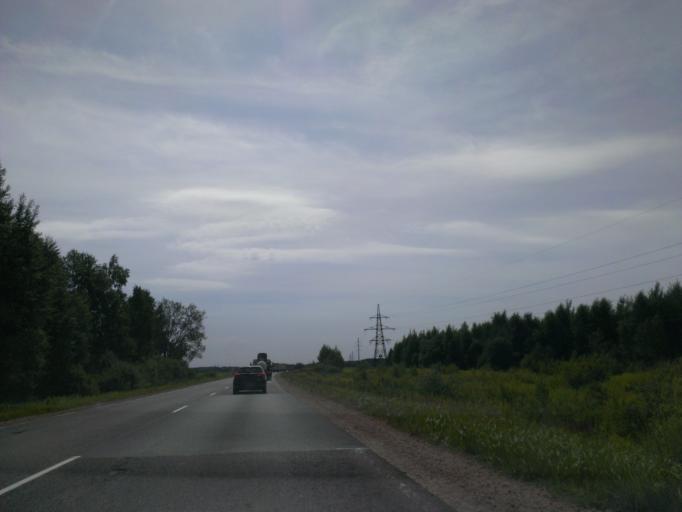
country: LV
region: Salaspils
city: Salaspils
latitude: 56.8658
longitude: 24.4065
